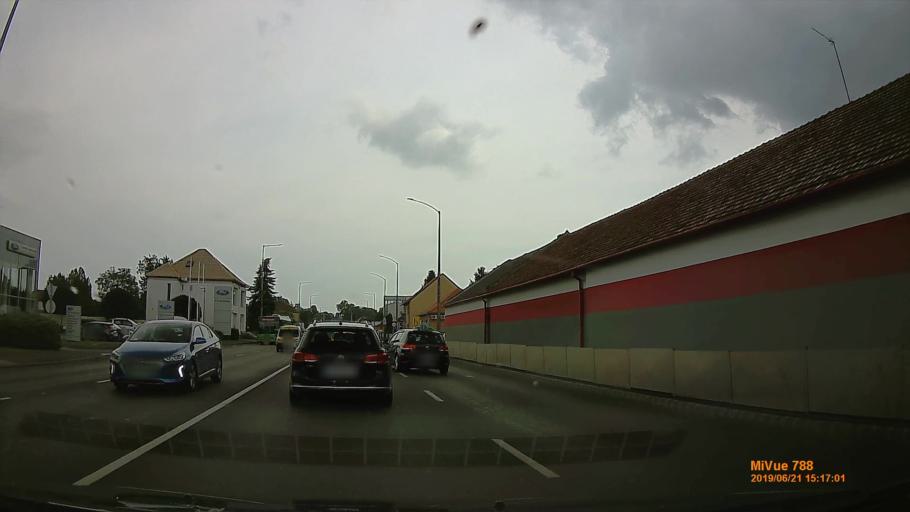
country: HU
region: Baranya
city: Pecs
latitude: 46.0597
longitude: 18.2305
